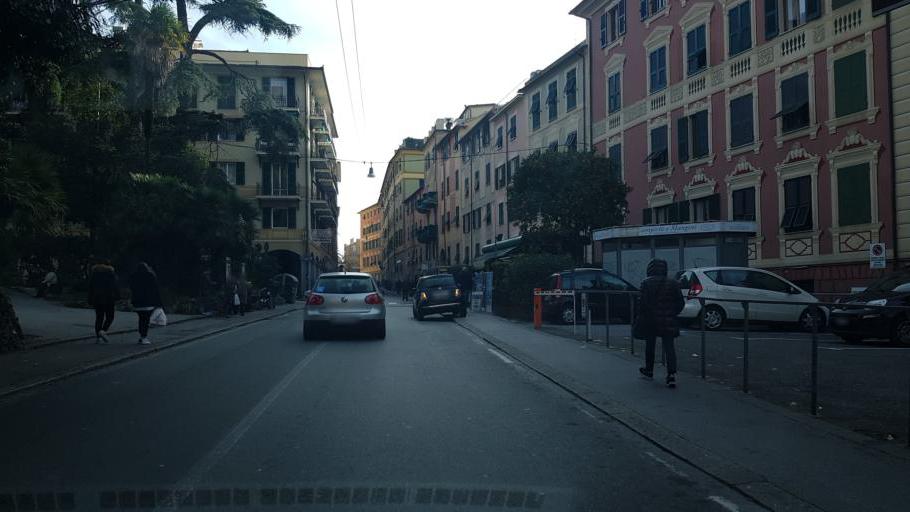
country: IT
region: Liguria
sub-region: Provincia di Genova
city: Bogliasco
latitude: 44.3846
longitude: 9.0351
